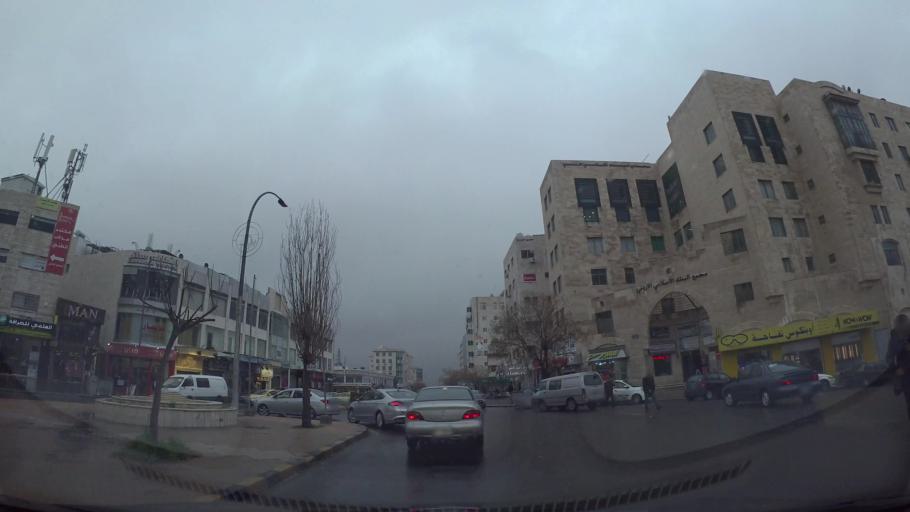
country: JO
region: Amman
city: Amman
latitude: 31.9696
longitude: 35.9148
